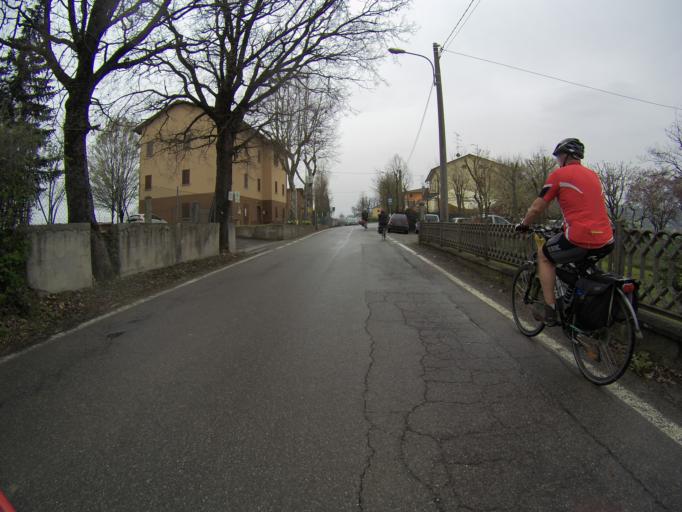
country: IT
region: Emilia-Romagna
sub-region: Provincia di Reggio Emilia
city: Ciano d'Enza
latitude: 44.5367
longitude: 10.4157
